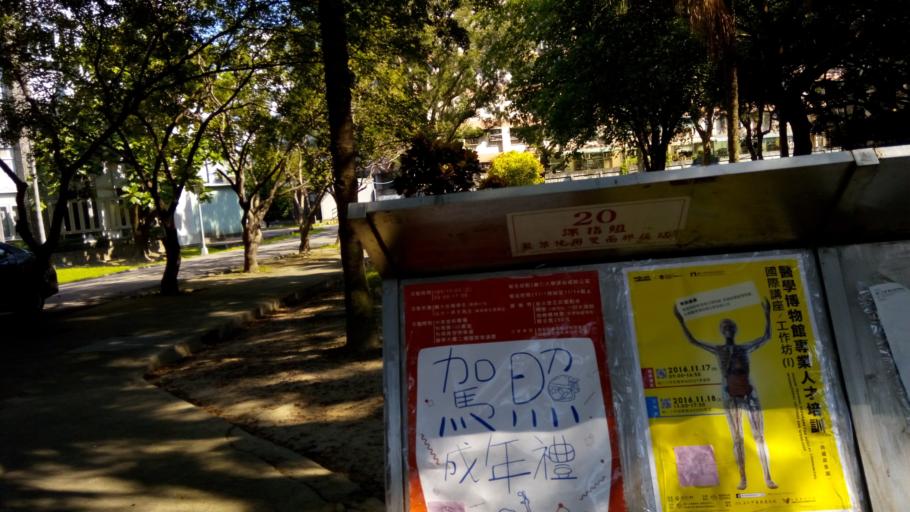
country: TW
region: Taipei
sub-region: Taipei
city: Banqiao
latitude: 25.0335
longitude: 121.4339
